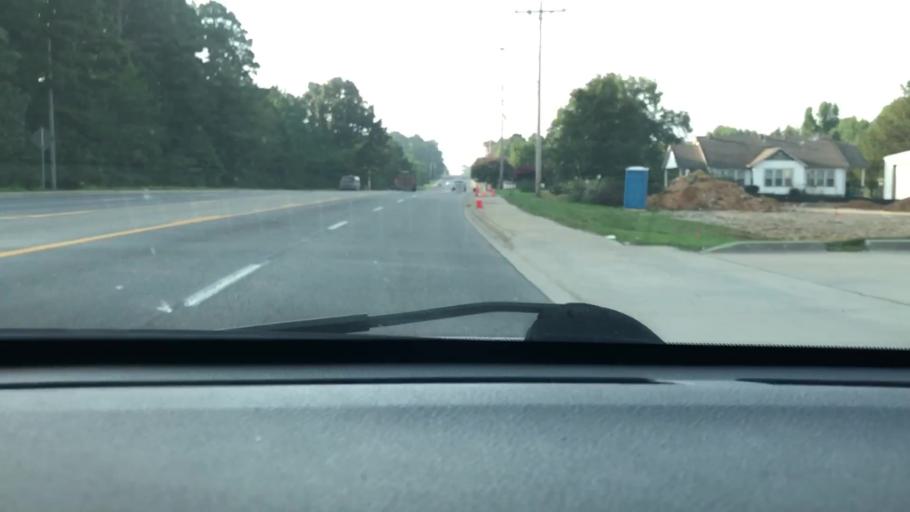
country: US
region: Arkansas
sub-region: Saline County
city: Bryant
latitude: 34.6086
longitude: -92.4926
